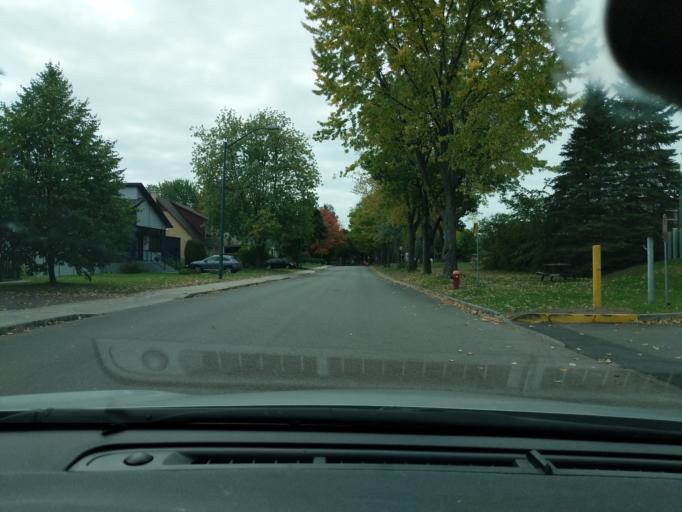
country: CA
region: Quebec
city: L'Ancienne-Lorette
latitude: 46.7675
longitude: -71.2813
